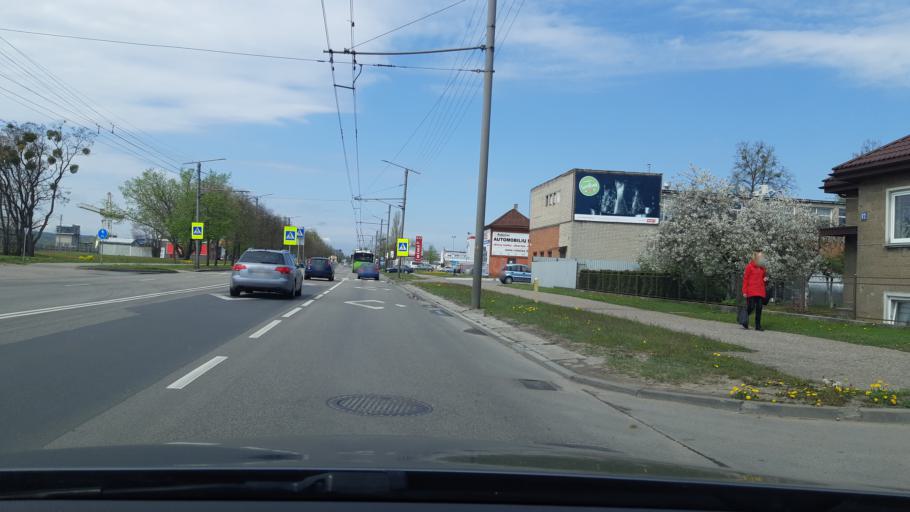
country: LT
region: Kauno apskritis
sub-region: Kaunas
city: Silainiai
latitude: 54.9081
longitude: 23.8684
